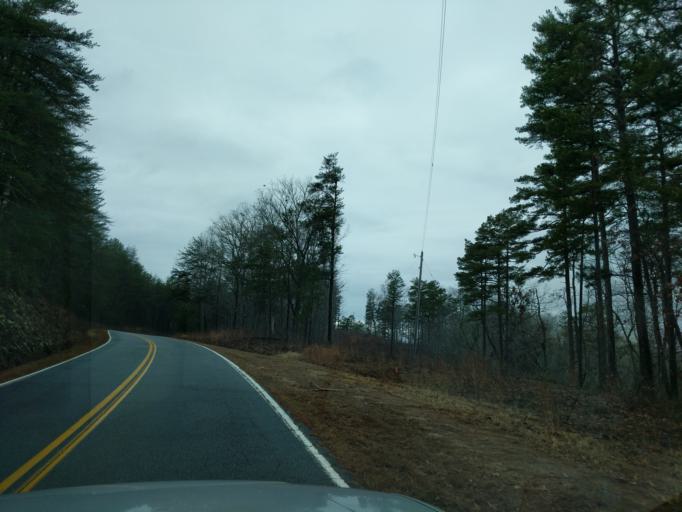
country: US
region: South Carolina
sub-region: Oconee County
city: Walhalla
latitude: 34.7882
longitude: -83.1906
